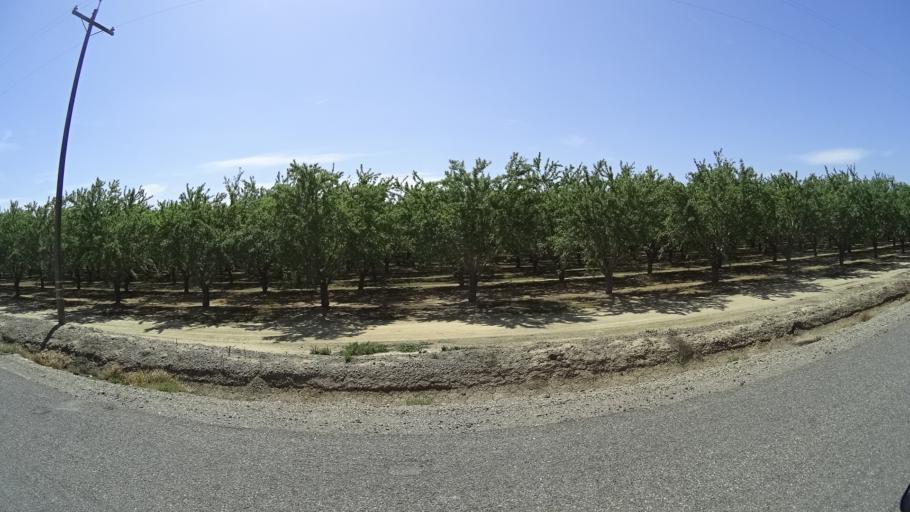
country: US
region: California
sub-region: Glenn County
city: Hamilton City
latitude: 39.6524
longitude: -122.0723
